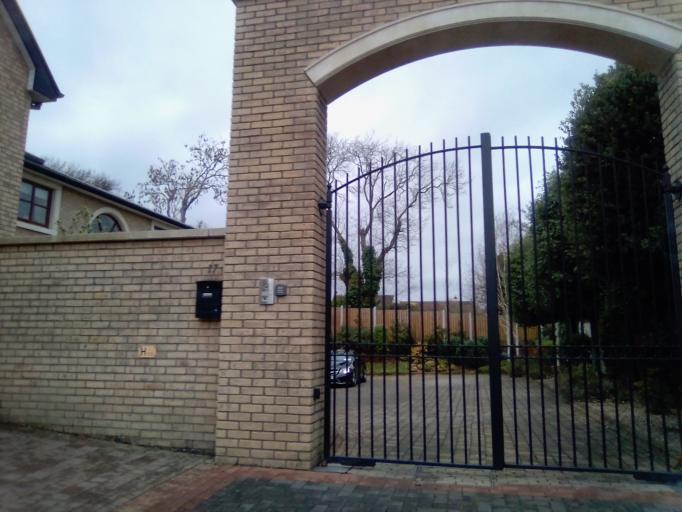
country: IE
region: Leinster
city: Malahide
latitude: 53.4471
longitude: -6.1474
